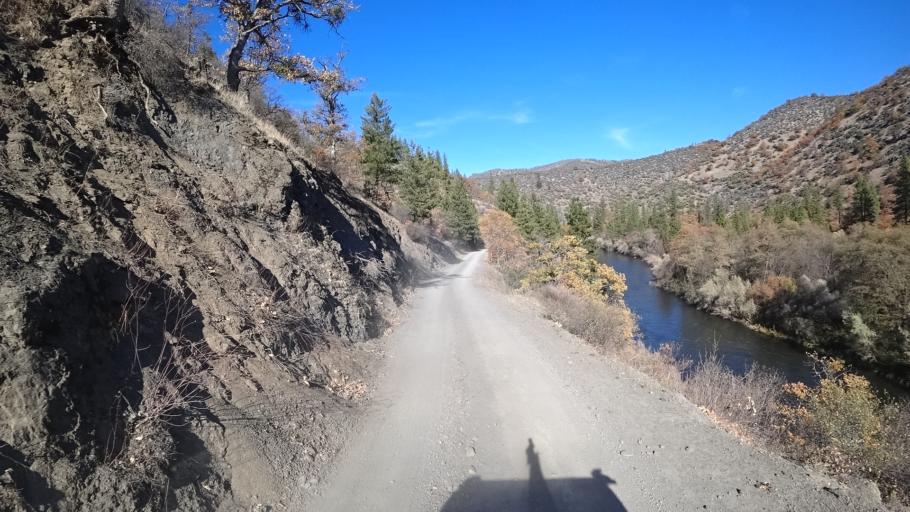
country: US
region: California
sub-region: Siskiyou County
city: Yreka
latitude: 41.8503
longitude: -122.6950
